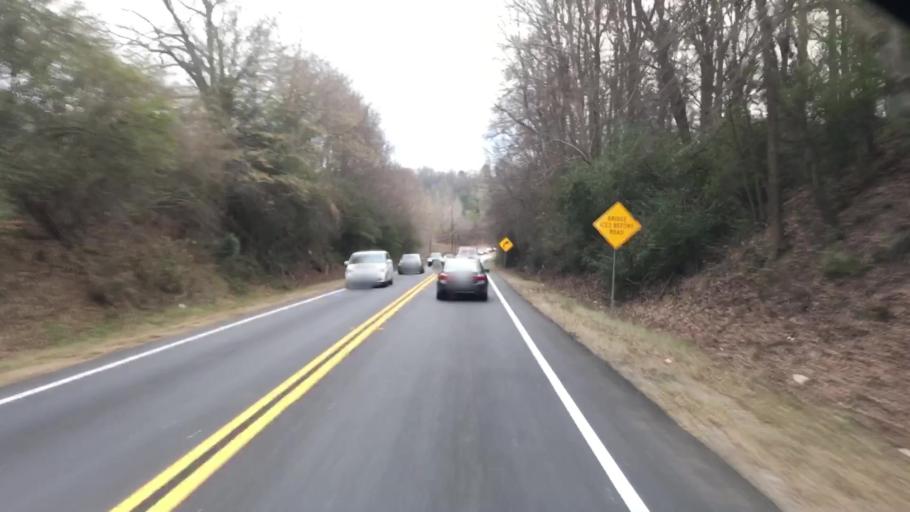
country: US
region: Georgia
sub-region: Jackson County
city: Braselton
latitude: 34.1115
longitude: -83.8177
